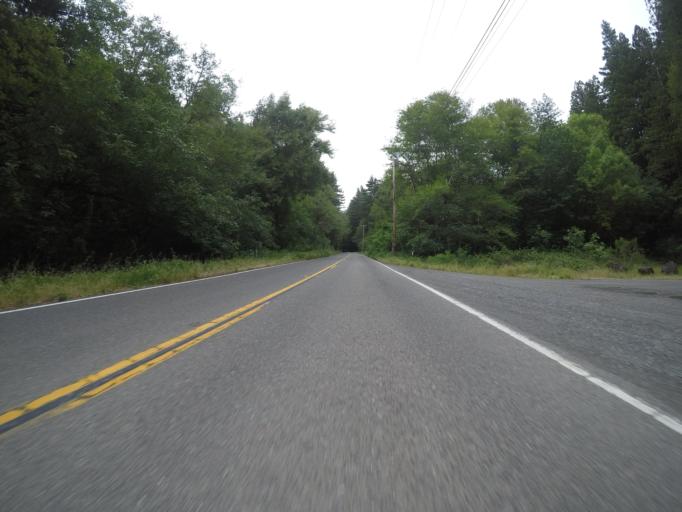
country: US
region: California
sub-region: Humboldt County
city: Rio Dell
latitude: 40.4129
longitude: -123.9592
